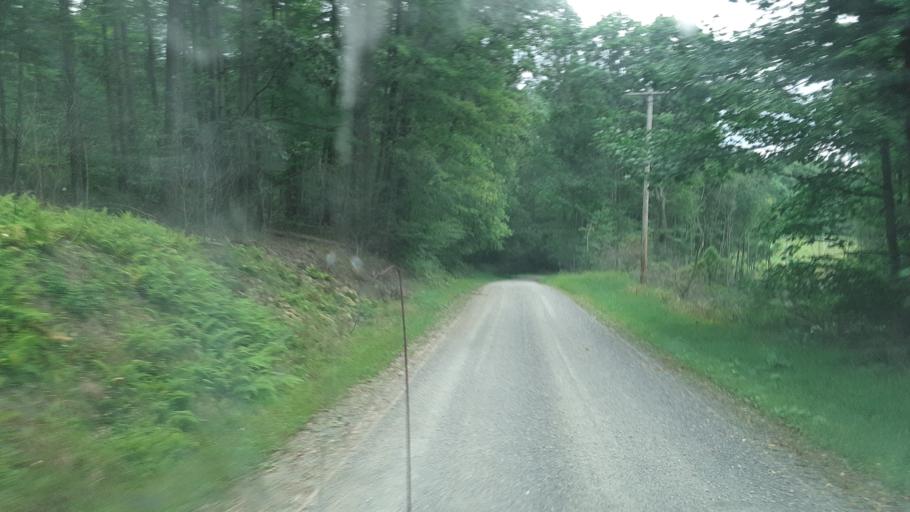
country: US
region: Pennsylvania
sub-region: Jefferson County
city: Punxsutawney
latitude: 40.9510
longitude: -79.1513
